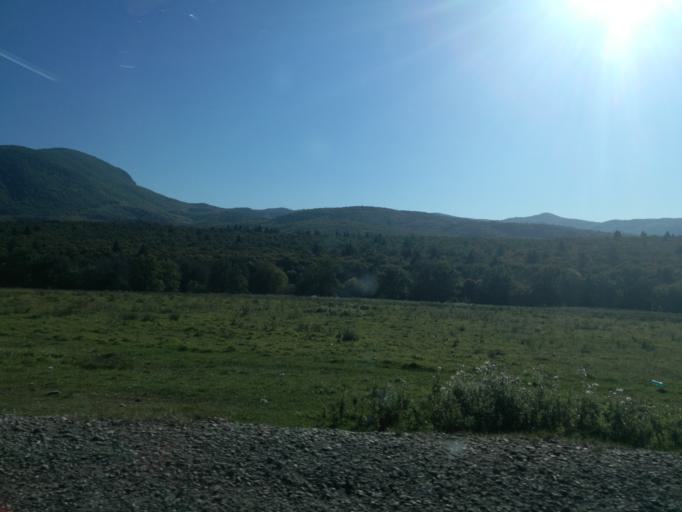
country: RO
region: Brasov
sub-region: Comuna Dumbravita
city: Dumbravita
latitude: 45.7502
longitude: 25.3985
